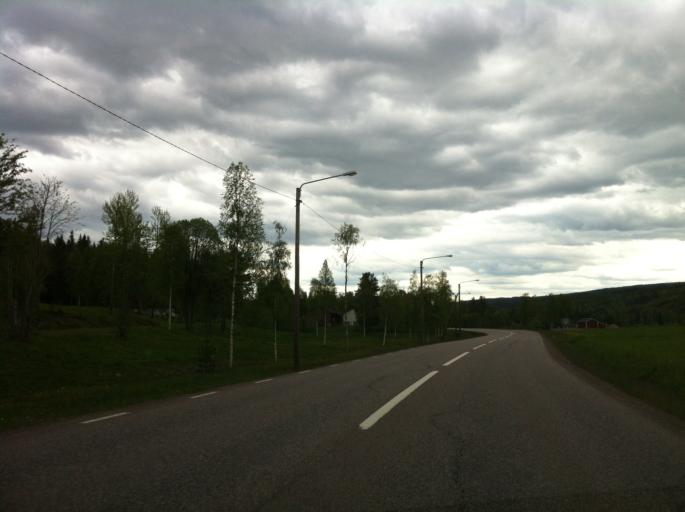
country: SE
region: Dalarna
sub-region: Malung-Saelens kommun
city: Malung
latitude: 61.1345
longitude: 13.2823
